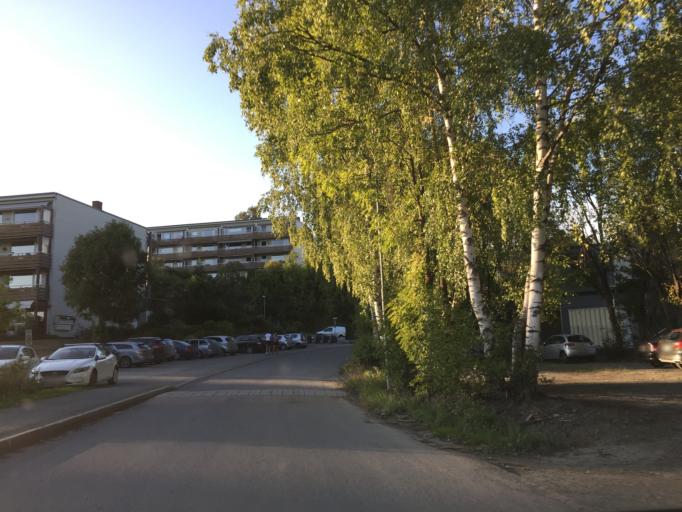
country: NO
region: Akershus
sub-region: Baerum
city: Lysaker
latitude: 59.9040
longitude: 10.6147
